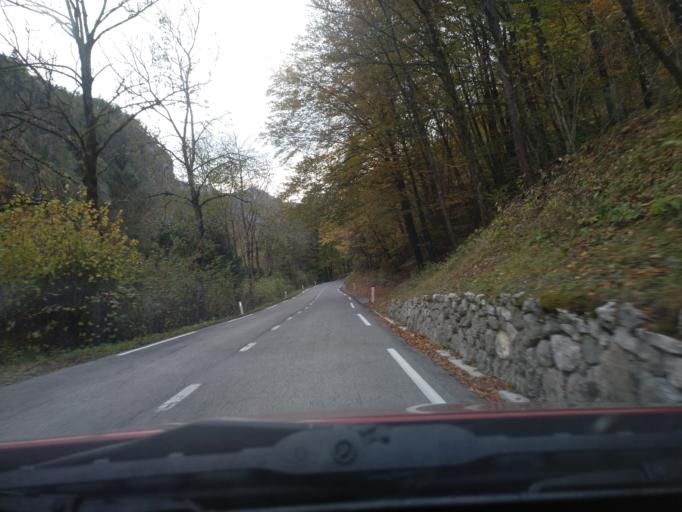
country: SI
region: Bovec
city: Bovec
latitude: 46.3345
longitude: 13.5960
